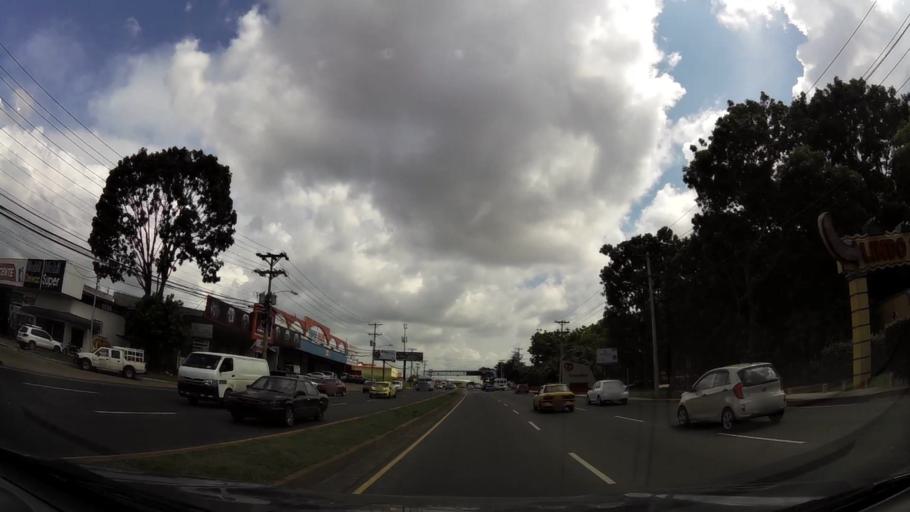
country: PA
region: Panama
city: San Miguelito
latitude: 9.0513
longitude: -79.4469
